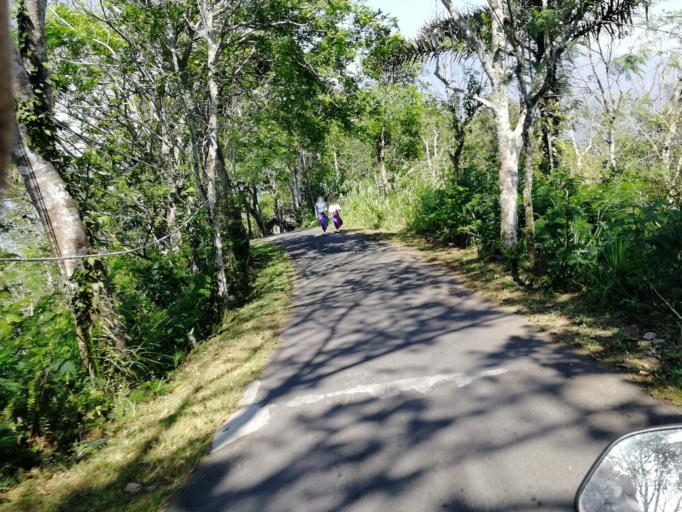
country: ID
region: Bali
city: Tiyingtali Kelod
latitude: -8.3923
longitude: 115.6341
